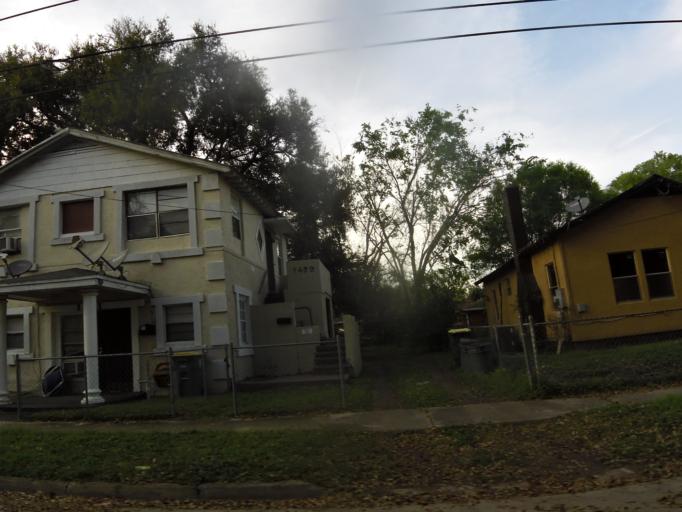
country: US
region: Florida
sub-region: Duval County
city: Jacksonville
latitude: 30.3547
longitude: -81.6797
